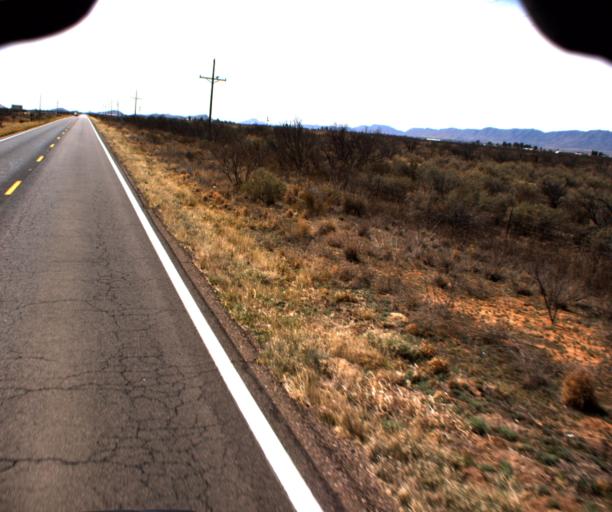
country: US
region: Arizona
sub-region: Cochise County
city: Willcox
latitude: 32.0012
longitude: -109.8616
